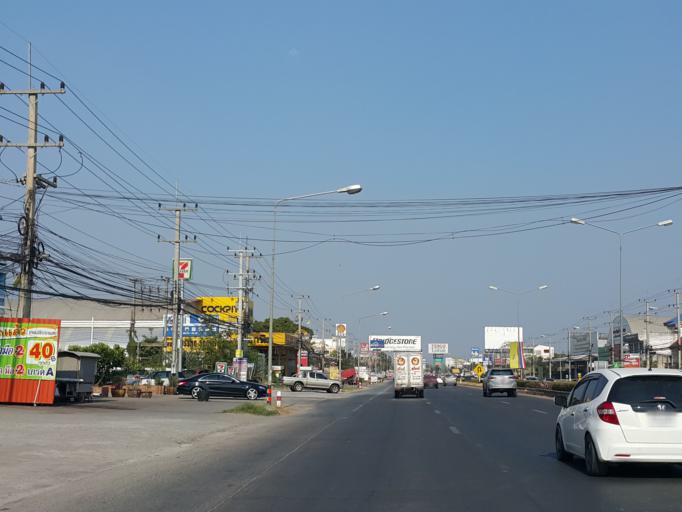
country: TH
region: Phitsanulok
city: Phitsanulok
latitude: 16.8183
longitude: 100.2905
